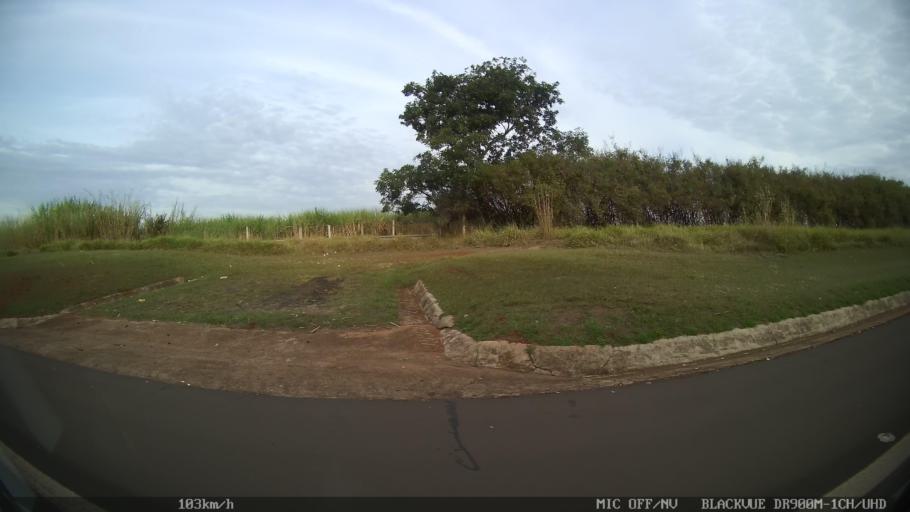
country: BR
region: Sao Paulo
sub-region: Iracemapolis
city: Iracemapolis
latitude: -22.6652
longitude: -47.5344
